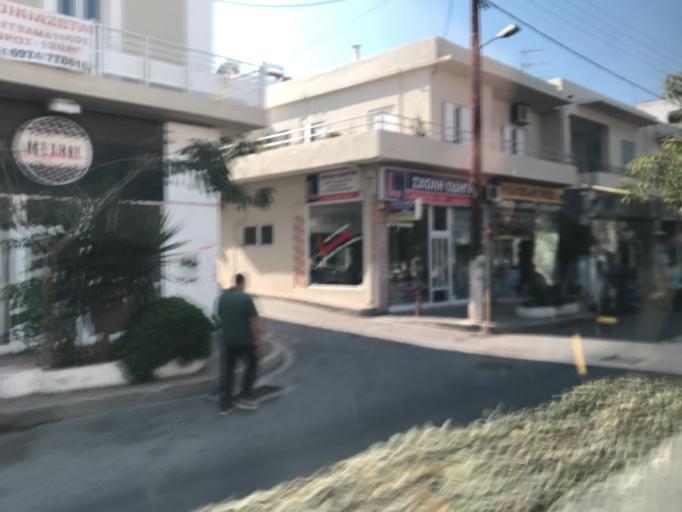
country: GR
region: Crete
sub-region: Nomos Irakleiou
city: Irakleion
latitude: 35.3357
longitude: 25.1191
